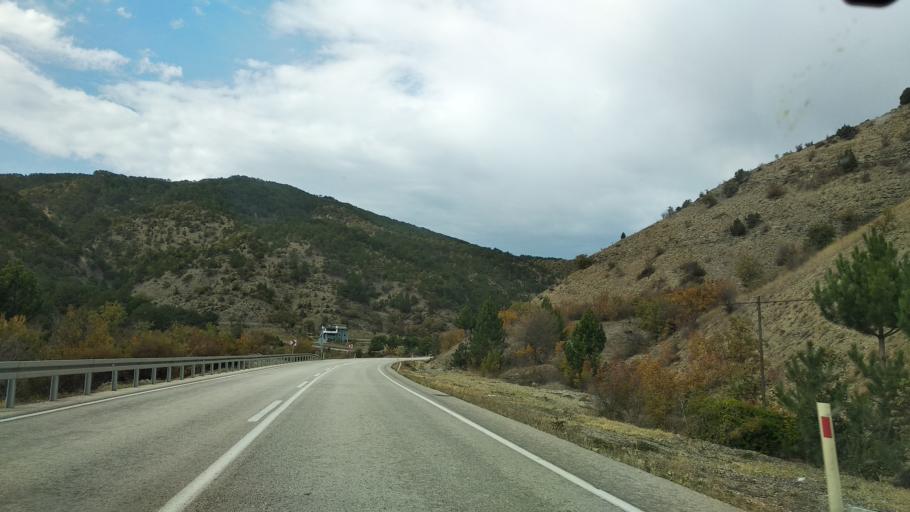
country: TR
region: Bolu
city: Mudurnu
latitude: 40.3389
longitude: 31.2429
